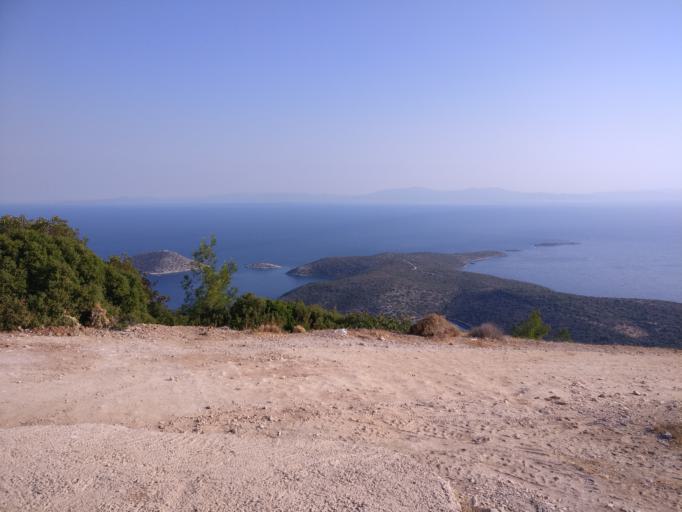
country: GR
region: North Aegean
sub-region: Nomos Samou
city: Samos
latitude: 37.7702
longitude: 26.9760
